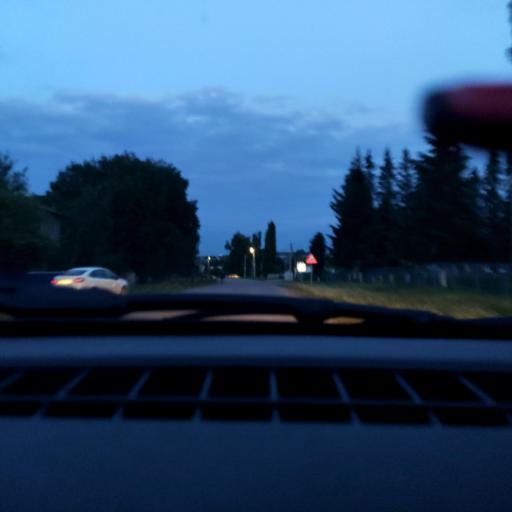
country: RU
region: Bashkortostan
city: Tolbazy
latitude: 54.2919
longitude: 55.8138
